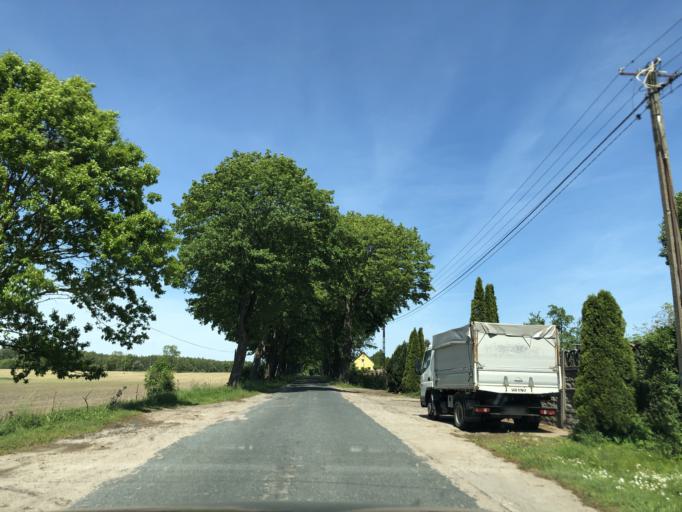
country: PL
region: West Pomeranian Voivodeship
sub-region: Powiat kolobrzeski
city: Goscino
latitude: 54.0133
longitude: 15.7330
